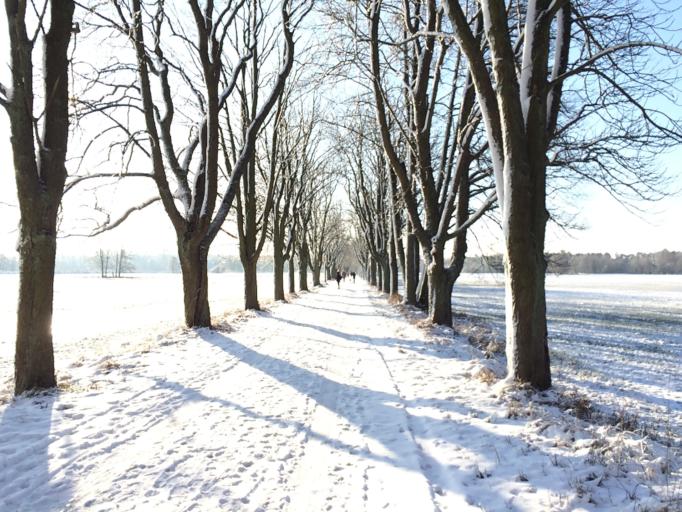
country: DE
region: Hesse
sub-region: Regierungsbezirk Darmstadt
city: Nauheim
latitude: 49.9848
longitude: 8.5107
